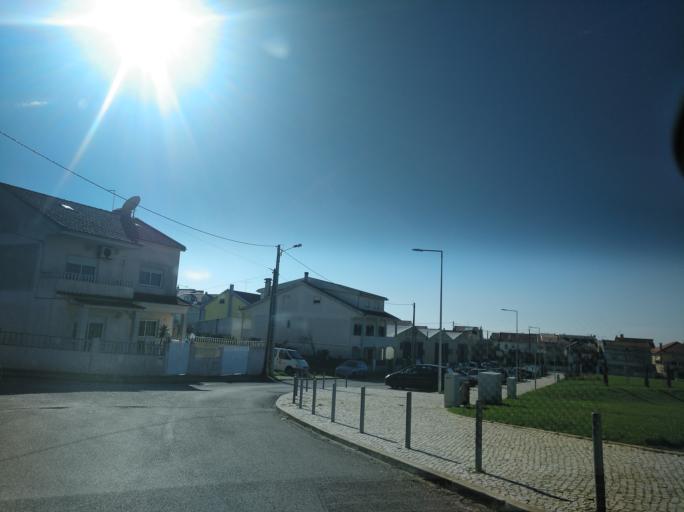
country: PT
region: Lisbon
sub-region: Odivelas
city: Canecas
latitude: 38.8064
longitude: -9.2182
